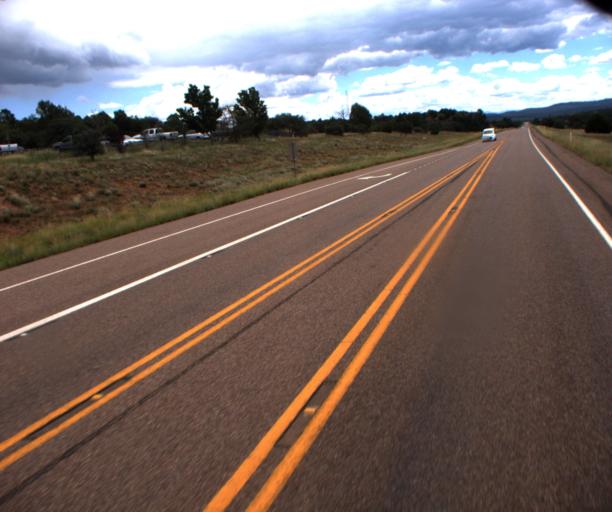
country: US
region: Arizona
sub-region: Navajo County
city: Linden
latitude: 34.3366
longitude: -110.2734
